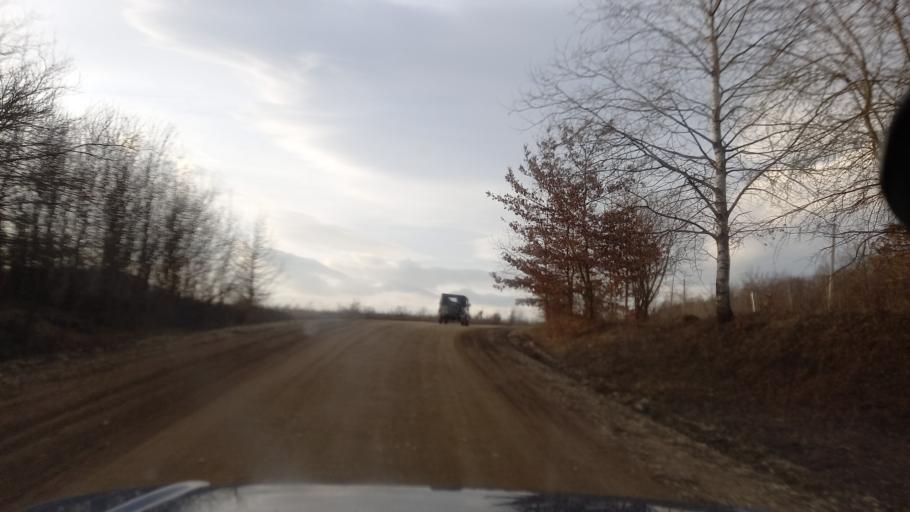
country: RU
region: Adygeya
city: Kamennomostskiy
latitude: 44.1939
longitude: 40.2566
